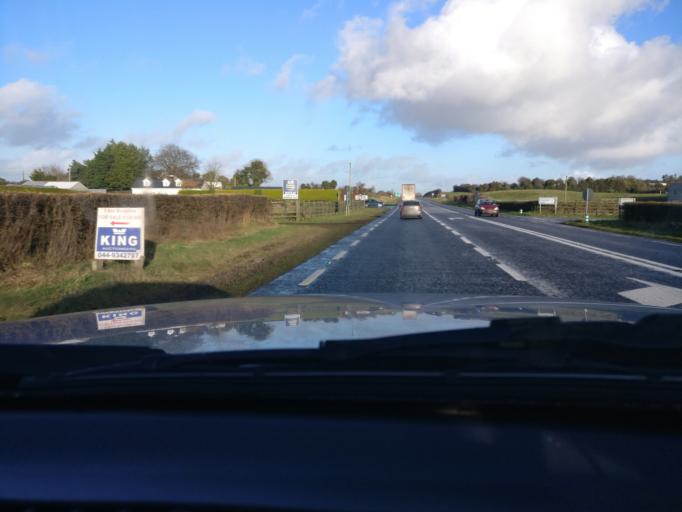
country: IE
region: Leinster
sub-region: An Iarmhi
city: Rathwire
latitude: 53.5954
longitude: -7.1144
